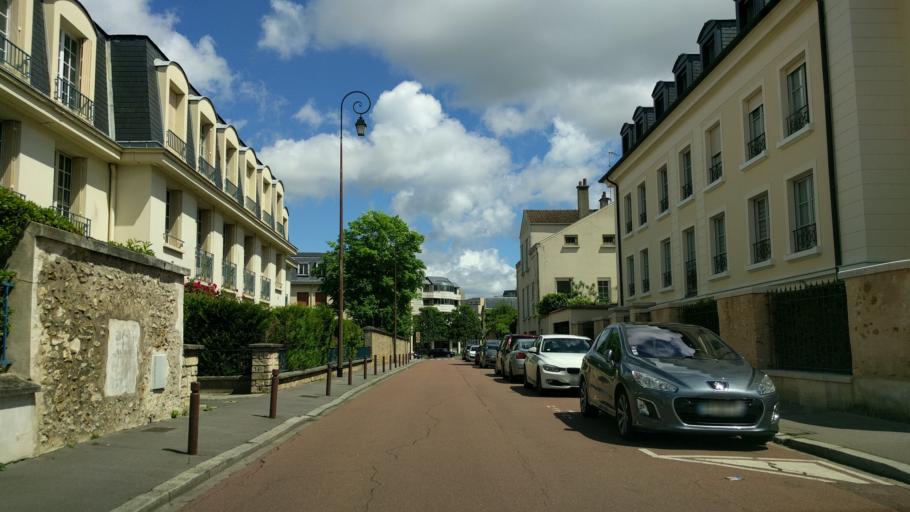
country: FR
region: Ile-de-France
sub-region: Departement des Yvelines
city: Le Chesnay
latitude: 48.8159
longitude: 2.1236
